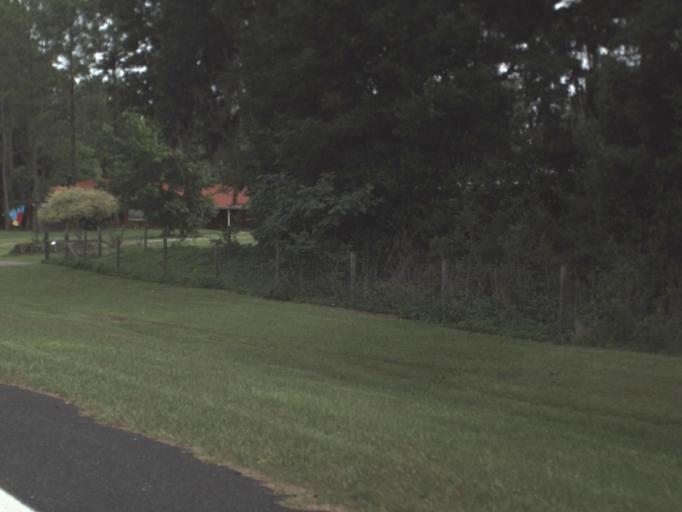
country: US
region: Florida
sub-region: Levy County
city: Williston
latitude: 29.3664
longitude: -82.4097
